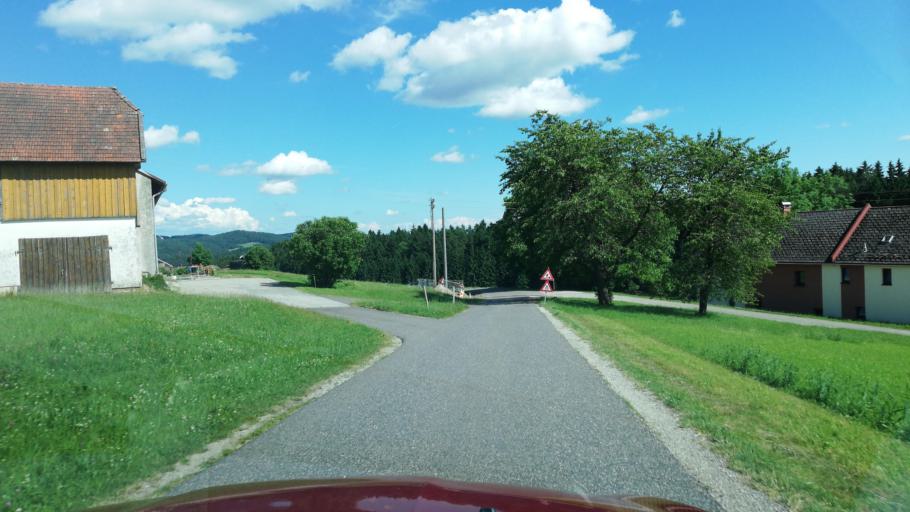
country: AT
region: Upper Austria
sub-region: Politischer Bezirk Urfahr-Umgebung
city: Reichenau im Muhlkreis
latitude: 48.4649
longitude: 14.3309
